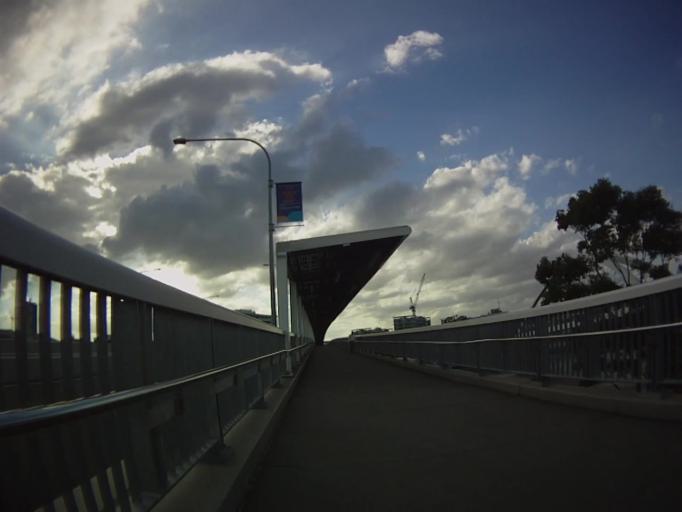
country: AU
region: Queensland
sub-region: Brisbane
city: Milton
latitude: -27.4707
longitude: 153.0133
